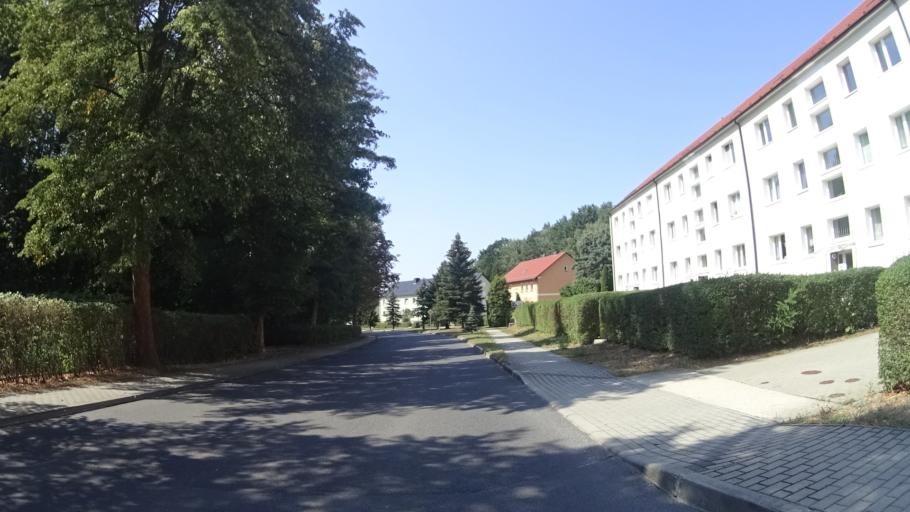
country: DE
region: Saxony
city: Gross Duben
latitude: 51.6032
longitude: 14.5794
